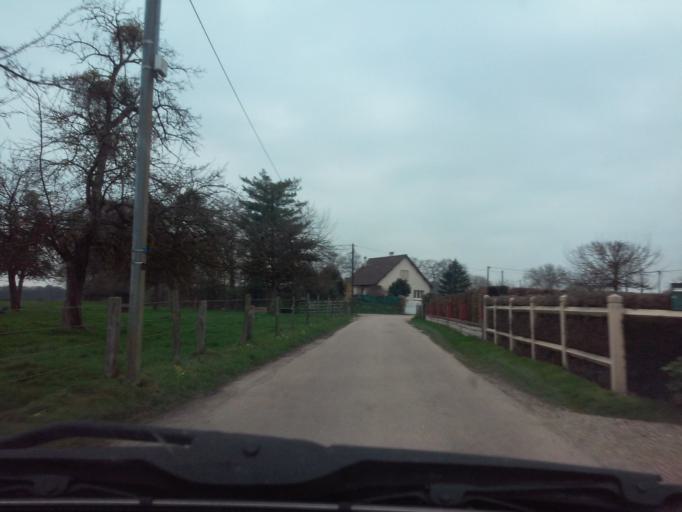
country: FR
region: Haute-Normandie
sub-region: Departement de la Seine-Maritime
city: Lanquetot
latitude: 49.5698
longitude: 0.5455
